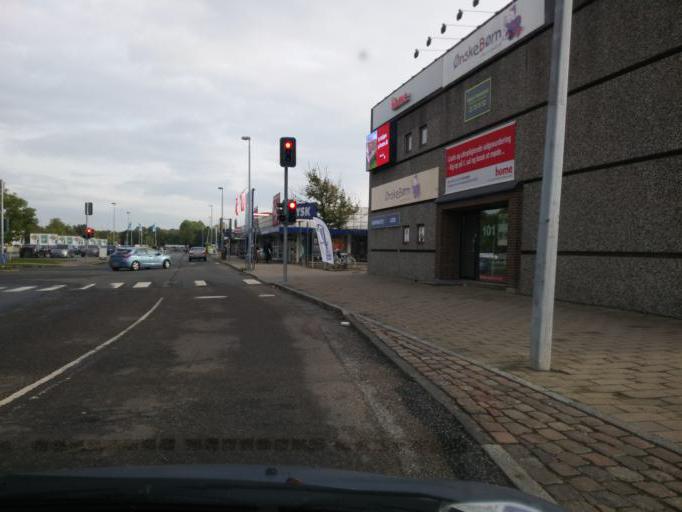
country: DK
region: South Denmark
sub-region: Odense Kommune
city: Neder Holluf
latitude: 55.3796
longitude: 10.4324
